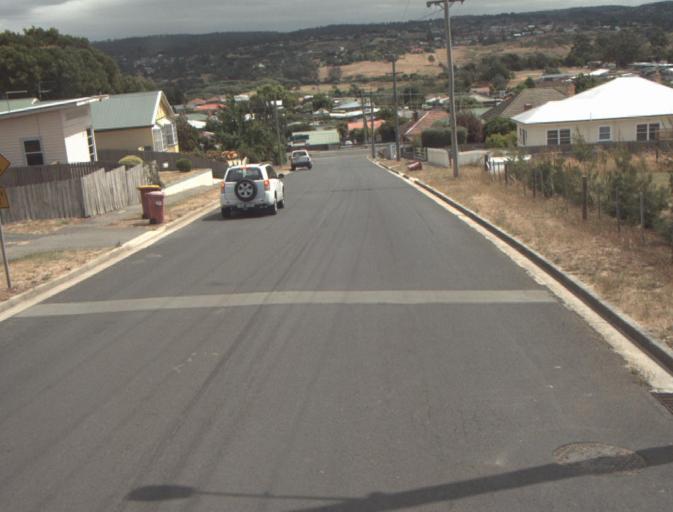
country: AU
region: Tasmania
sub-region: Launceston
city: Newstead
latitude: -41.4530
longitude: 147.1987
